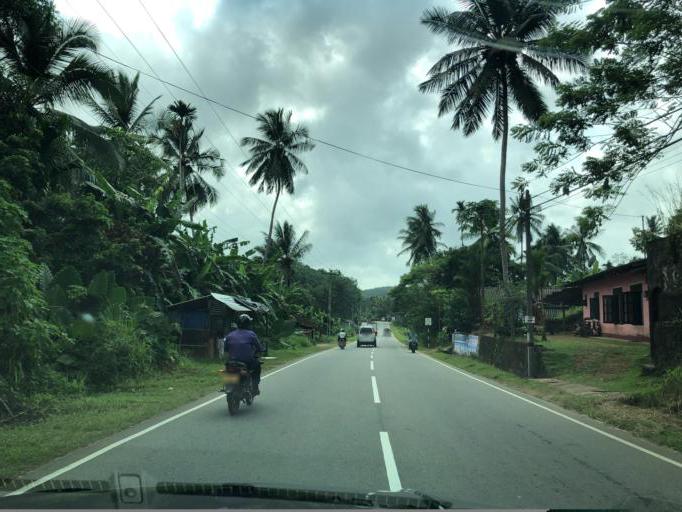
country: LK
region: Western
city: Horana South
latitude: 6.6783
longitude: 80.1528
